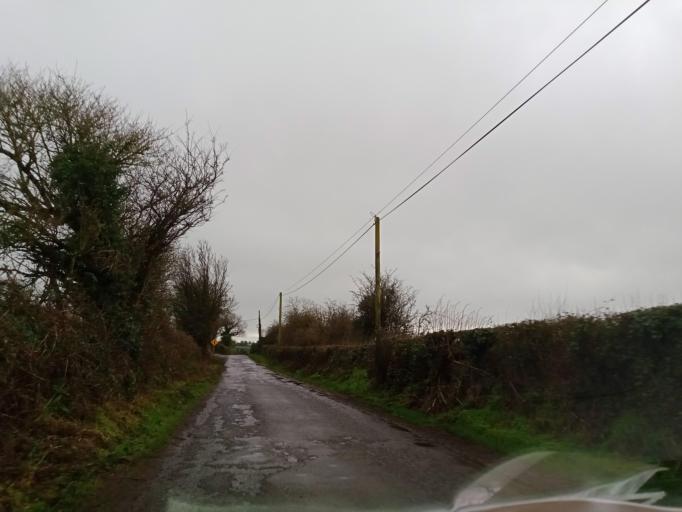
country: IE
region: Munster
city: Fethard
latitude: 52.5630
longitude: -7.7152
